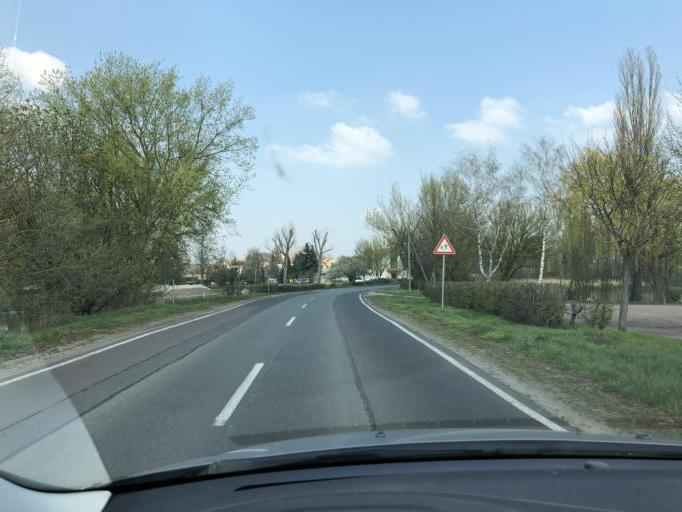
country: DE
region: Saxony-Anhalt
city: Zorbig
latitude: 51.6222
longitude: 12.1214
